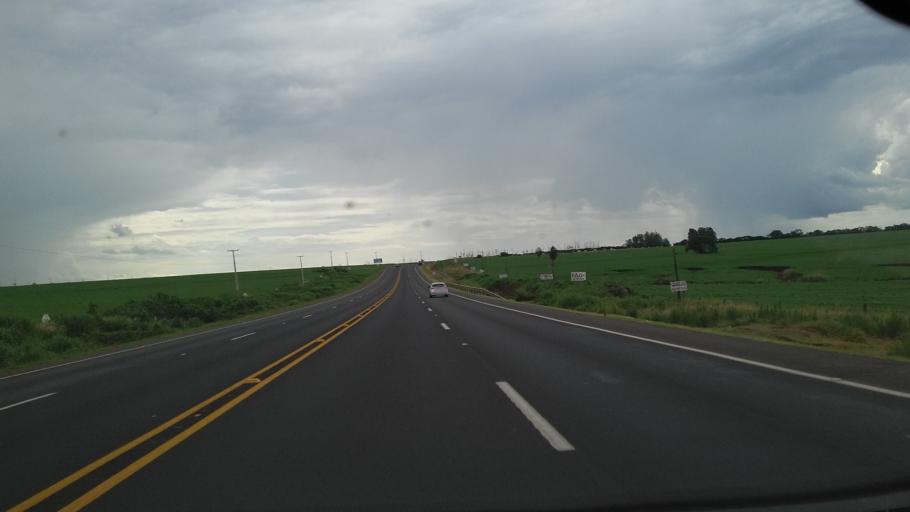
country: BR
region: Parana
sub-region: Arapongas
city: Arapongas
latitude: -23.4133
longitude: -51.4734
